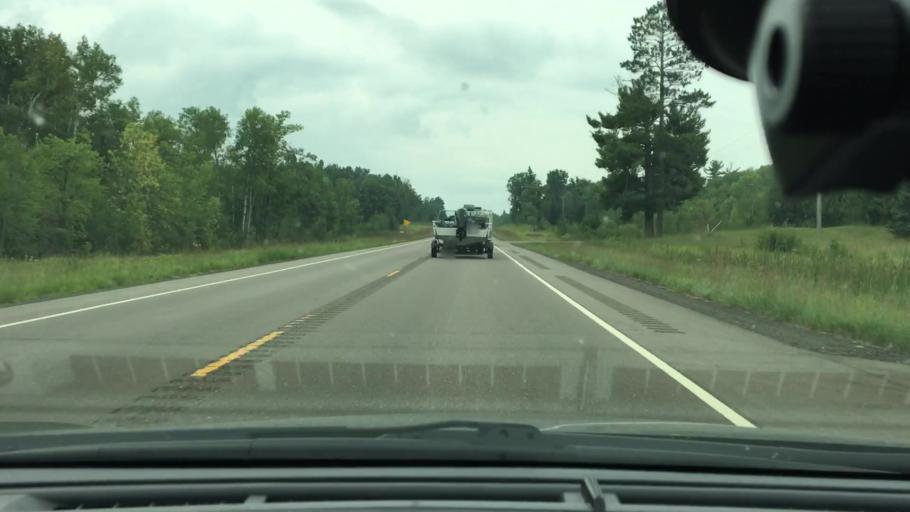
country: US
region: Minnesota
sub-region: Crow Wing County
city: Crosby
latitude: 46.5783
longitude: -93.9527
